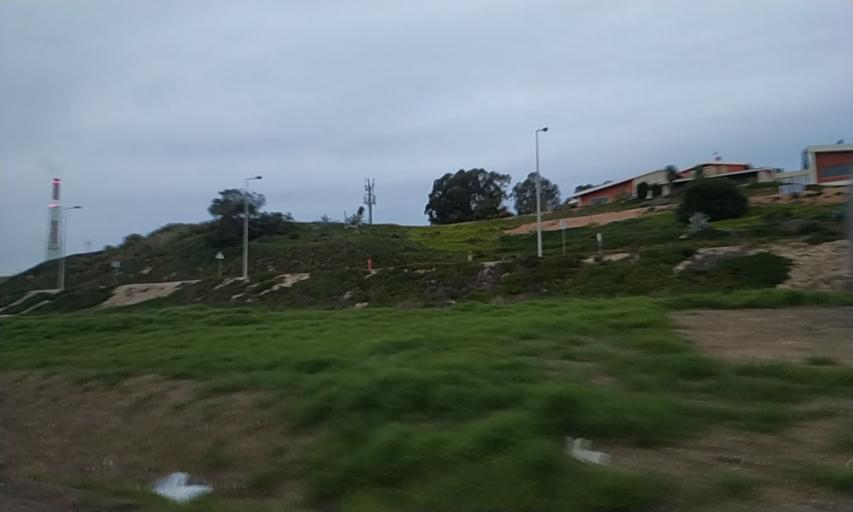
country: PT
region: Setubal
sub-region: Setubal
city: Setubal
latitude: 38.4957
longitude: -8.8340
